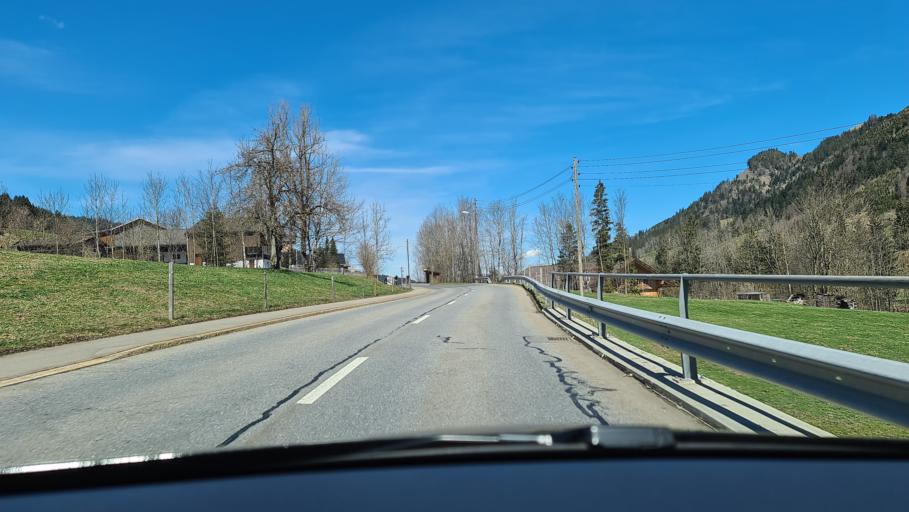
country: CH
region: Schwyz
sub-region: Bezirk Schwyz
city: Rothenthurm
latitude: 47.0856
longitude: 8.7216
